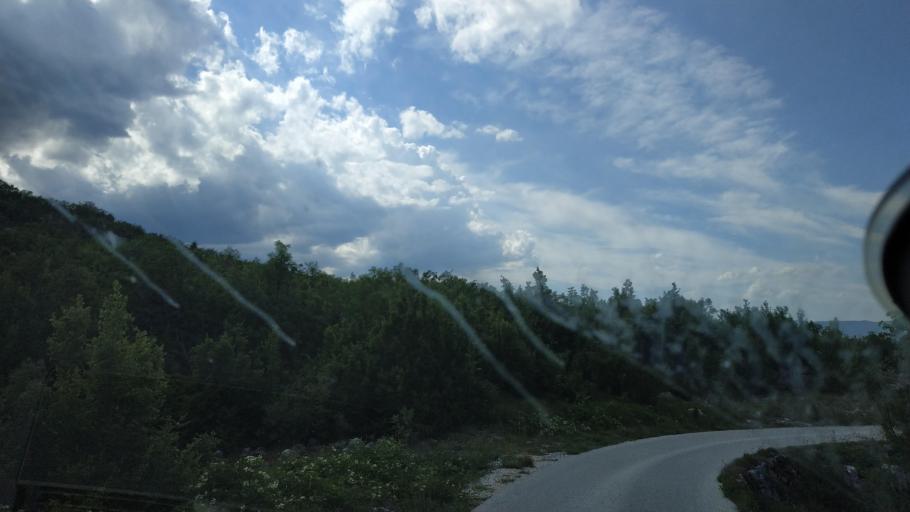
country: HR
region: Splitsko-Dalmatinska
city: Dugopolje
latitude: 43.5741
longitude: 16.6558
